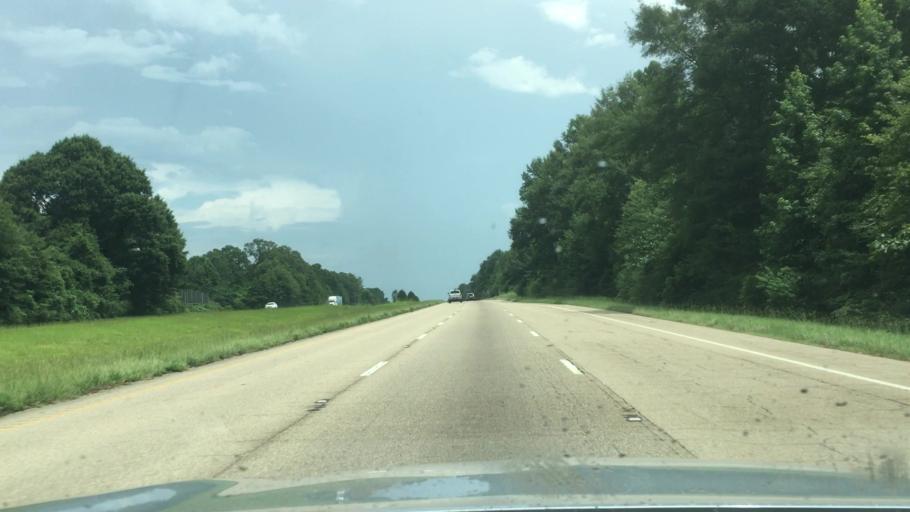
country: US
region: Mississippi
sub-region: Lamar County
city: Lumberton
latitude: 30.9263
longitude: -89.4566
